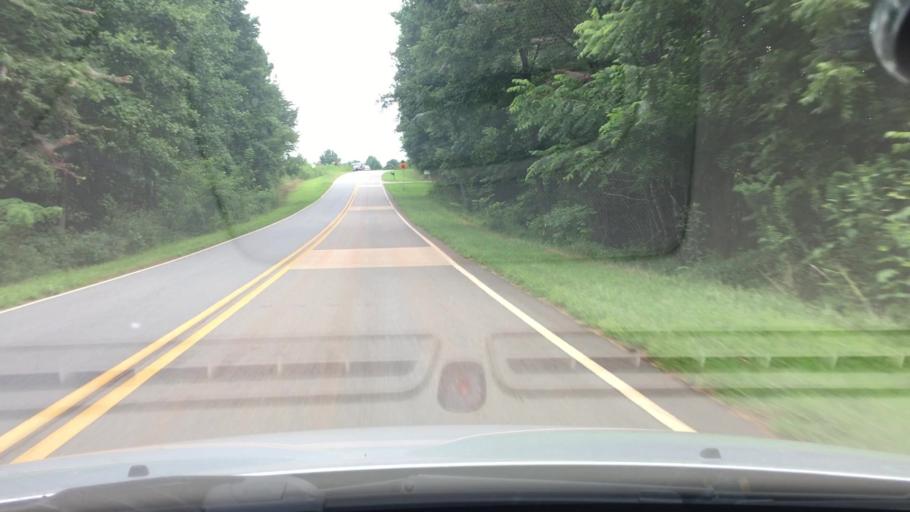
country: US
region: Georgia
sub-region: Lumpkin County
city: Dahlonega
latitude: 34.6061
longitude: -83.8974
